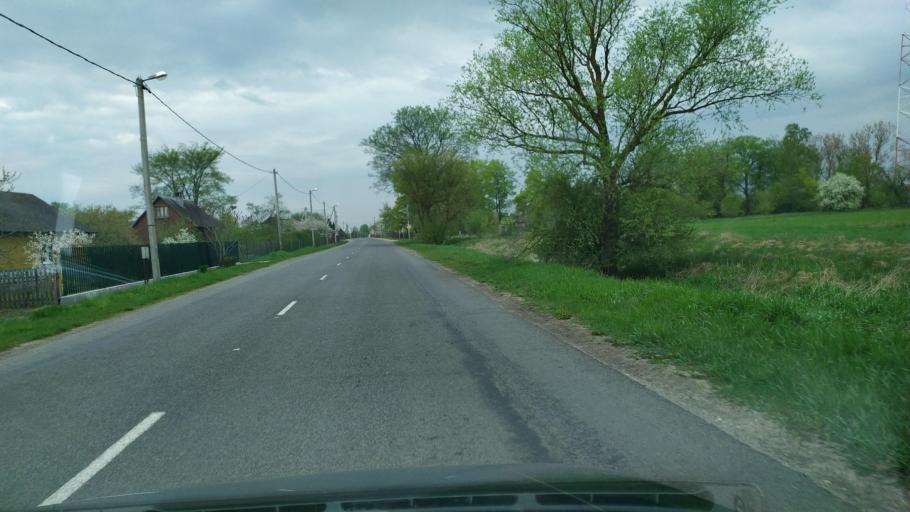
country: BY
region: Brest
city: Zhabinka
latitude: 52.1570
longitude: 24.0884
